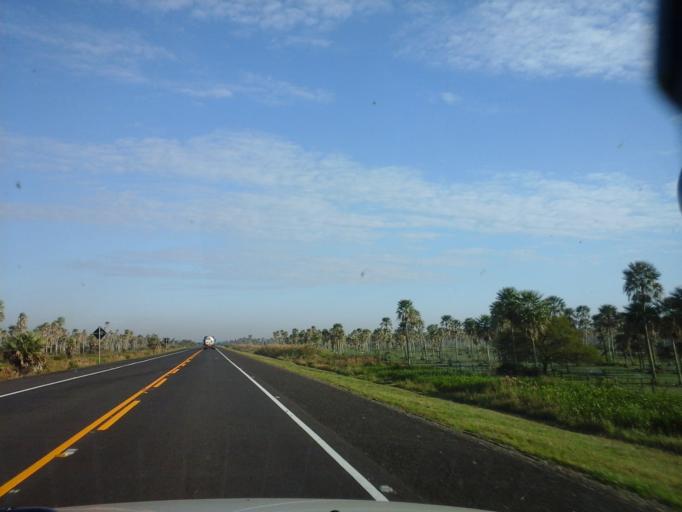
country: PY
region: Neembucu
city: Cerrito
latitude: -26.8908
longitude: -57.7251
